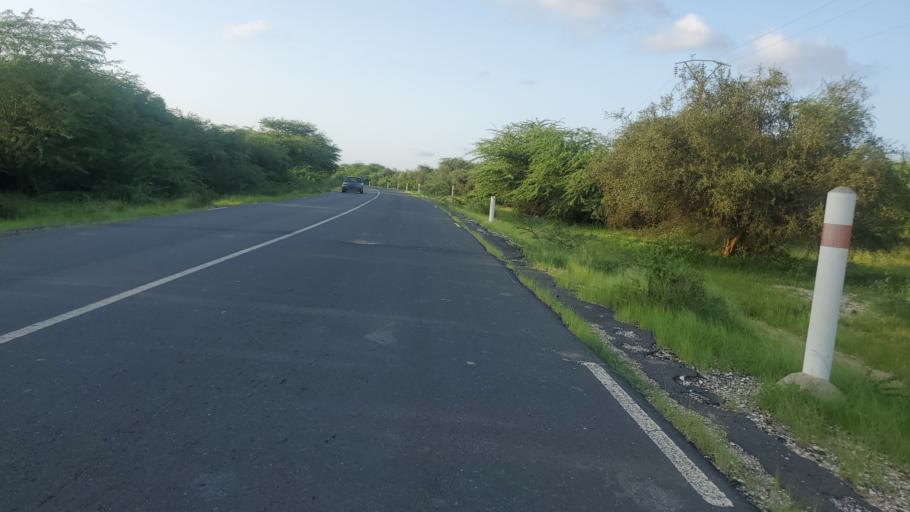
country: SN
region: Saint-Louis
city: Saint-Louis
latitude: 16.1944
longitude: -16.4091
